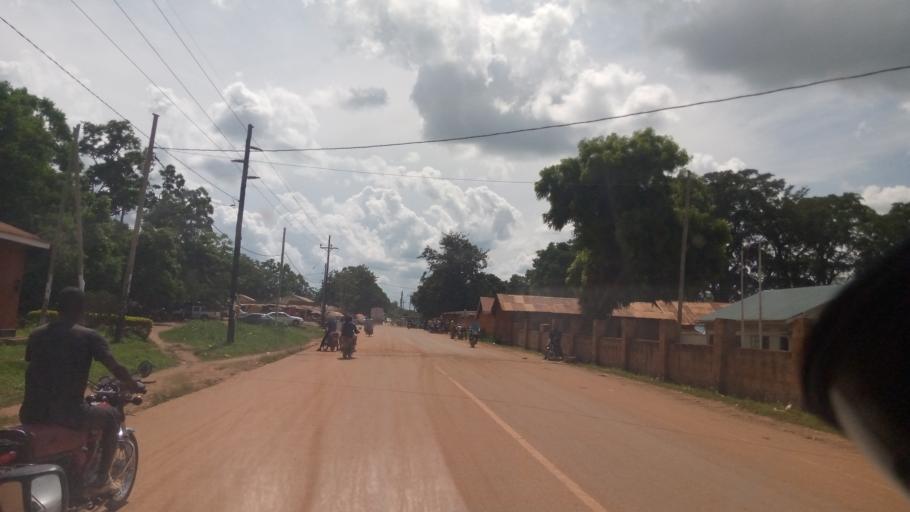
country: UG
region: Northern Region
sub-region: Lira District
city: Lira
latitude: 2.2498
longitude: 32.9031
